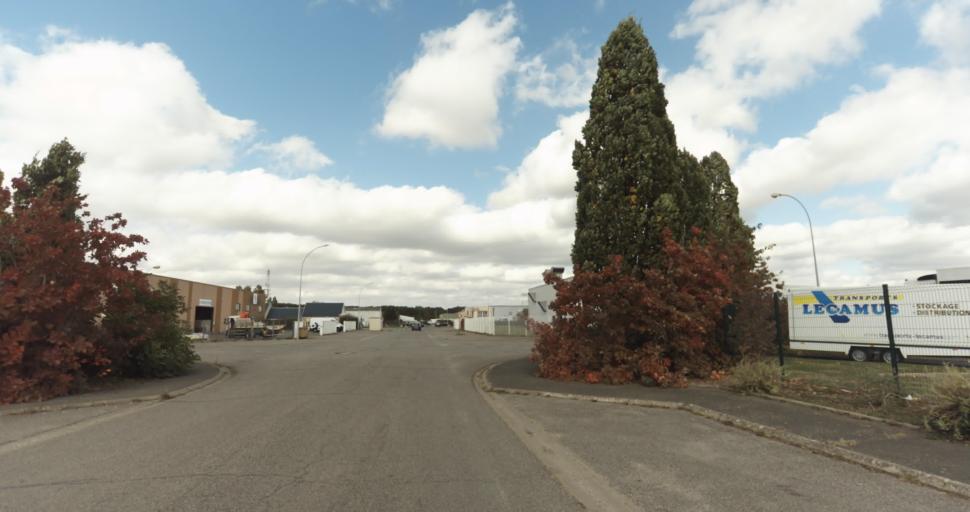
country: FR
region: Centre
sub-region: Departement d'Eure-et-Loir
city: Garnay
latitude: 48.7278
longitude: 1.3224
